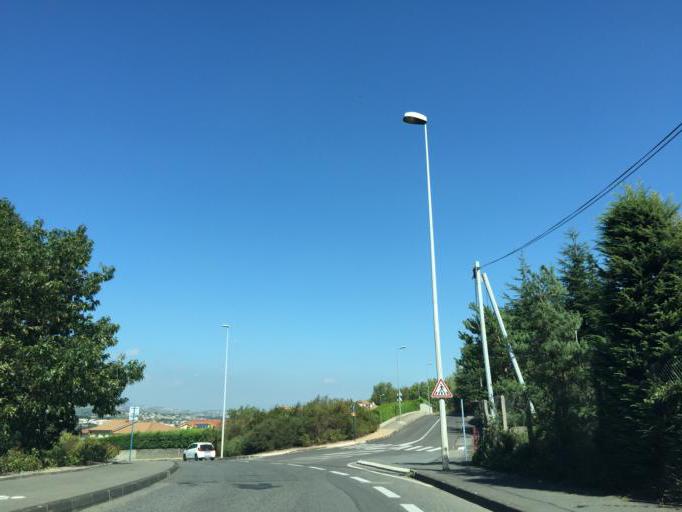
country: FR
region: Rhone-Alpes
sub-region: Departement de la Loire
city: Saint-Chamond
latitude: 45.4742
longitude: 4.5372
